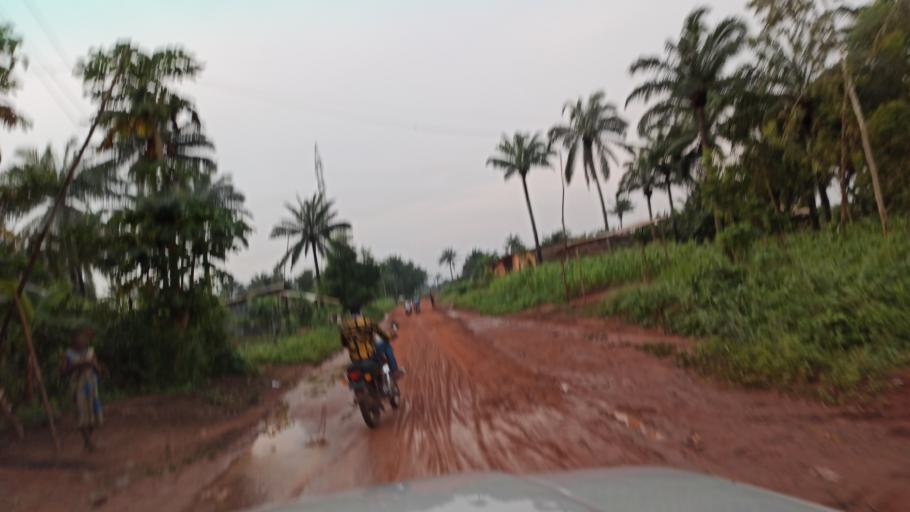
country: BJ
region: Queme
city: Porto-Novo
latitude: 6.5416
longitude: 2.6218
